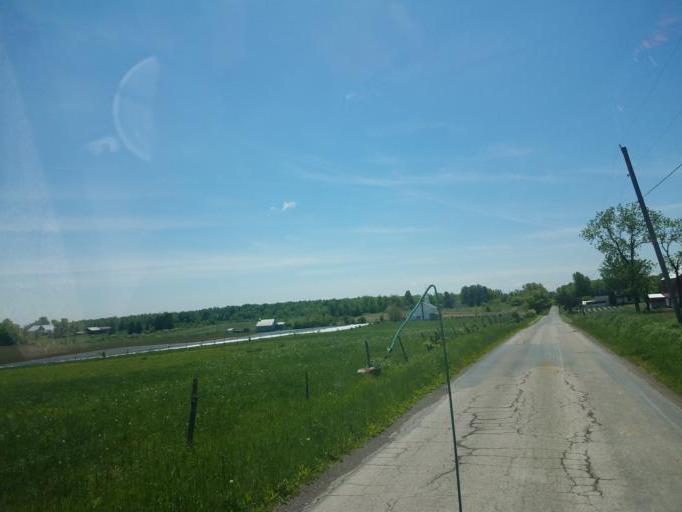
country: US
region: Ohio
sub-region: Wayne County
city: West Salem
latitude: 40.9767
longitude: -82.1772
